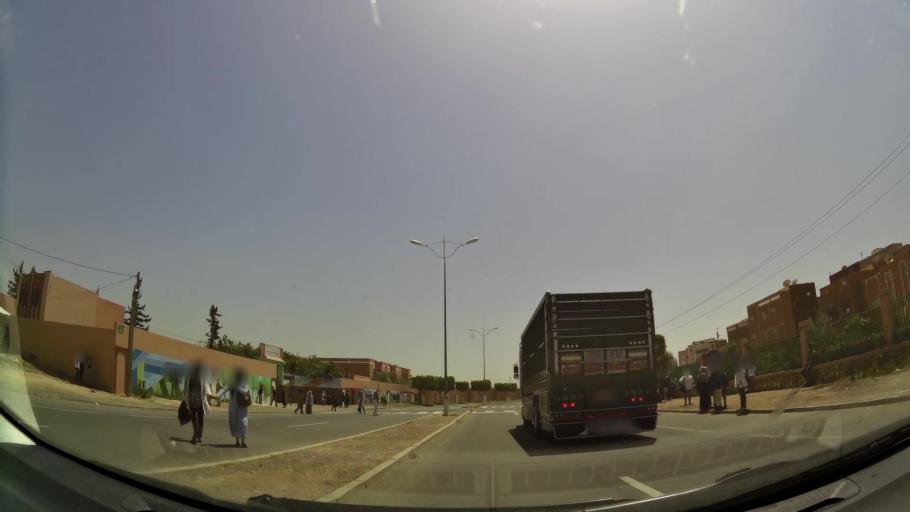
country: MA
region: Souss-Massa-Draa
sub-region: Inezgane-Ait Mellou
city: Inezgane
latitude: 30.3432
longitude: -9.4828
